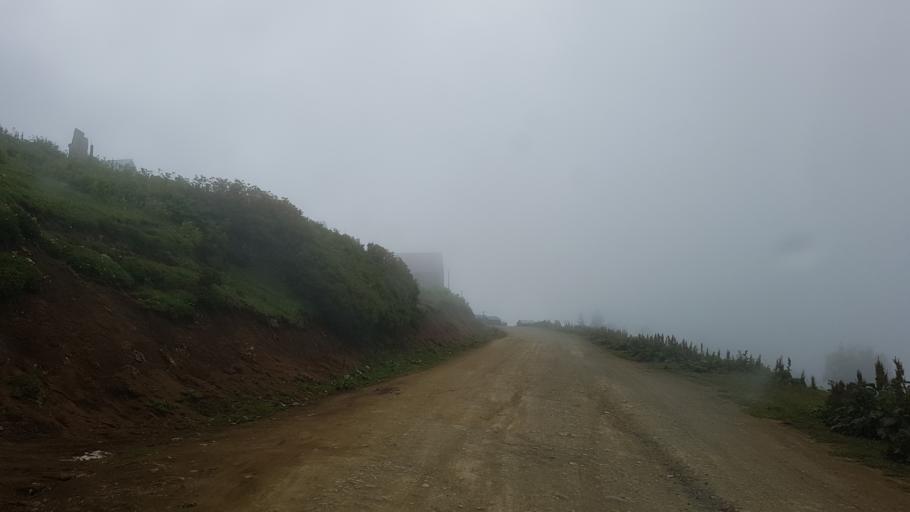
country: GE
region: Ajaria
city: Akhaldaba
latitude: 41.8236
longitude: 42.1574
